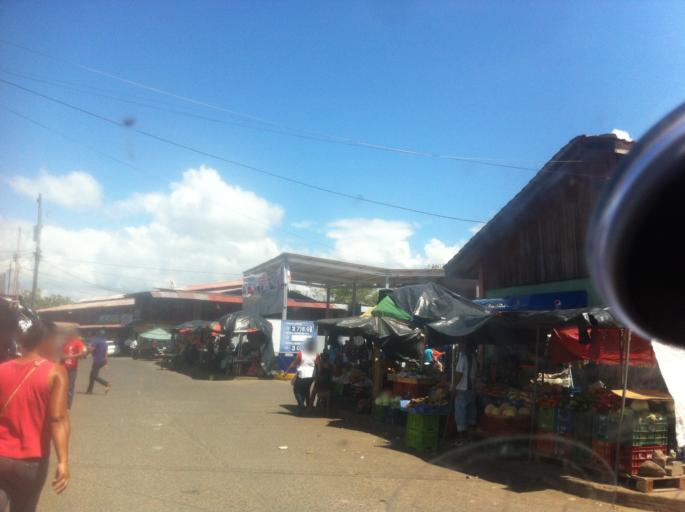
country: NI
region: Rio San Juan
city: San Carlos
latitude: 11.1231
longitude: -84.7763
